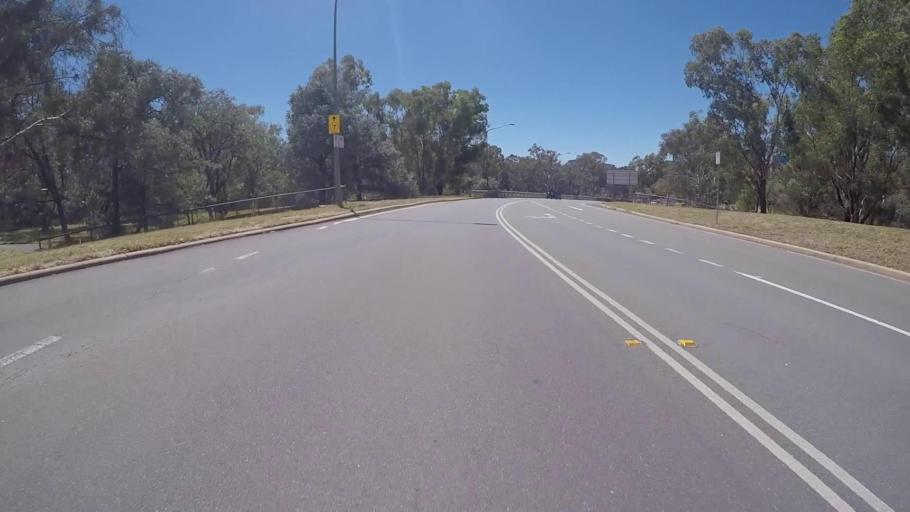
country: AU
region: Australian Capital Territory
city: Acton
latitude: -35.2874
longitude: 149.1185
